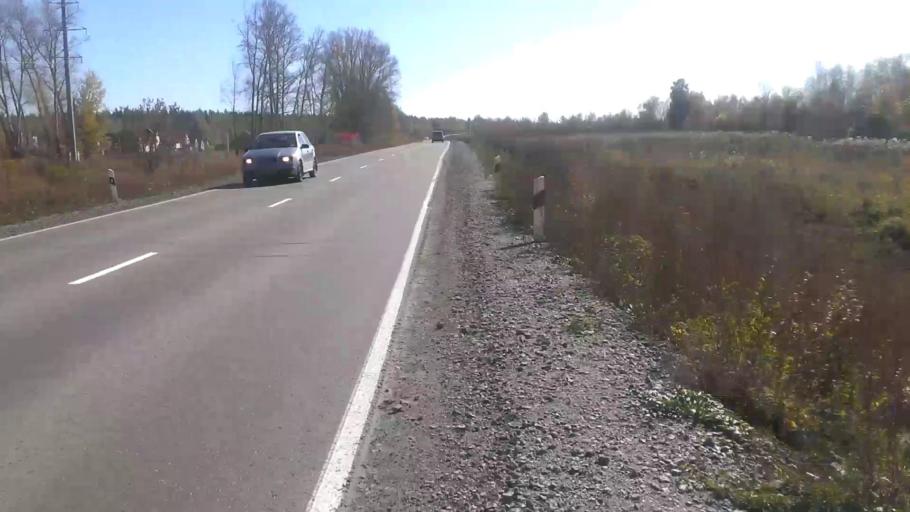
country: RU
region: Altai Krai
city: Sannikovo
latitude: 53.3086
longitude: 83.9674
